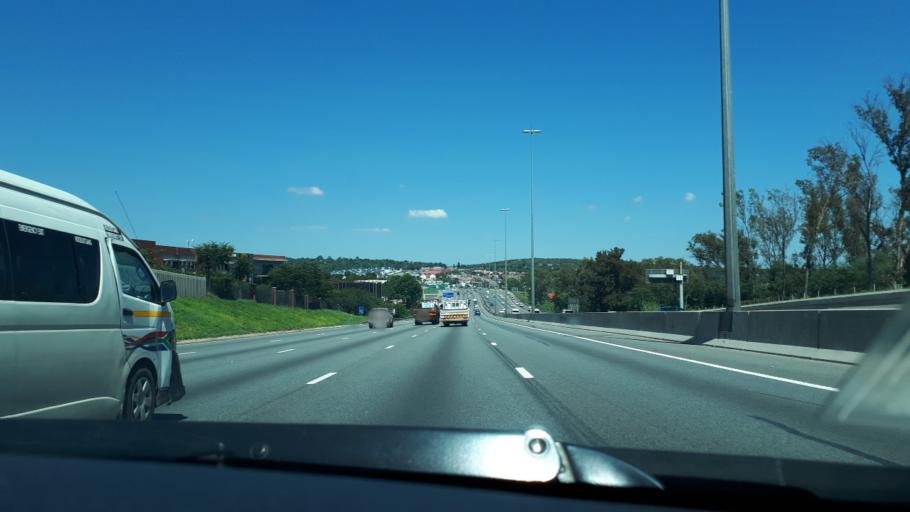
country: ZA
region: Gauteng
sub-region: City of Johannesburg Metropolitan Municipality
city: Midrand
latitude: -26.0397
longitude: 28.0688
